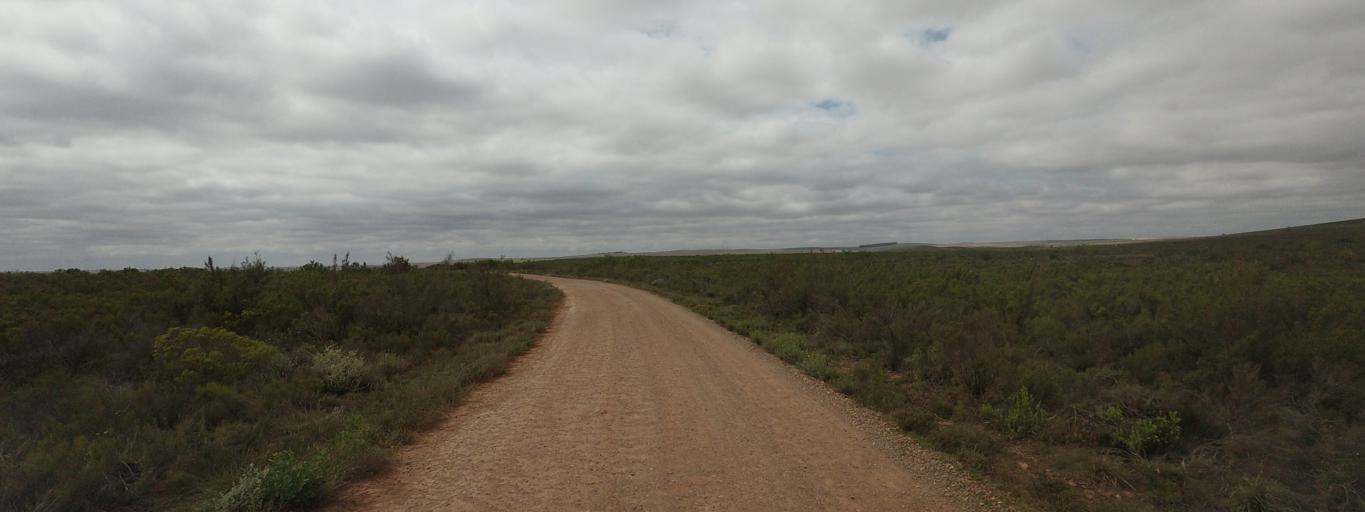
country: ZA
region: Western Cape
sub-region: Overberg District Municipality
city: Swellendam
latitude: -34.0613
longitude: 20.4332
